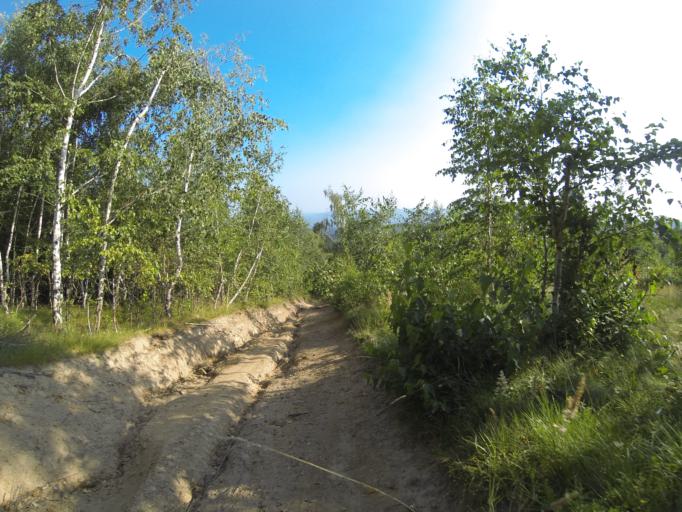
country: RO
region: Valcea
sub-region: Comuna Vaideeni
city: Vaideeni
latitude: 45.2030
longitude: 23.9783
